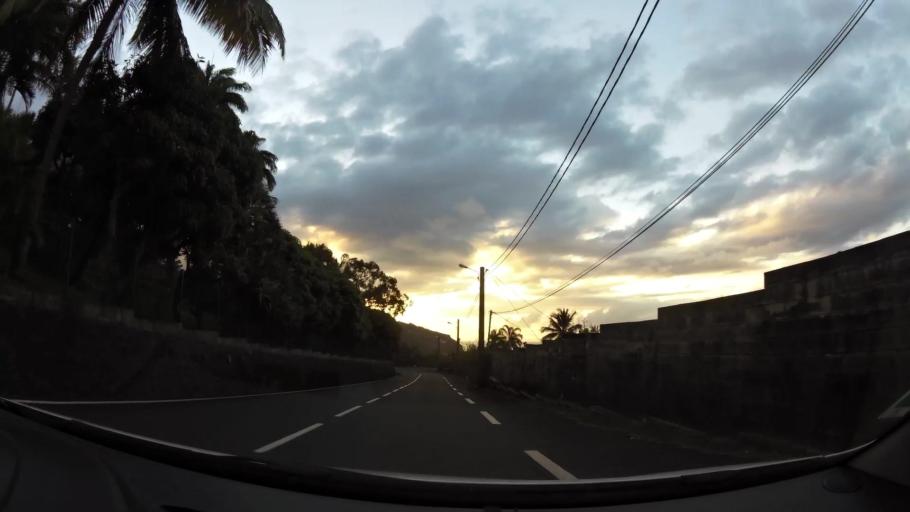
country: RE
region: Reunion
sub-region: Reunion
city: Saint-Denis
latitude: -20.9063
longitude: 55.4636
